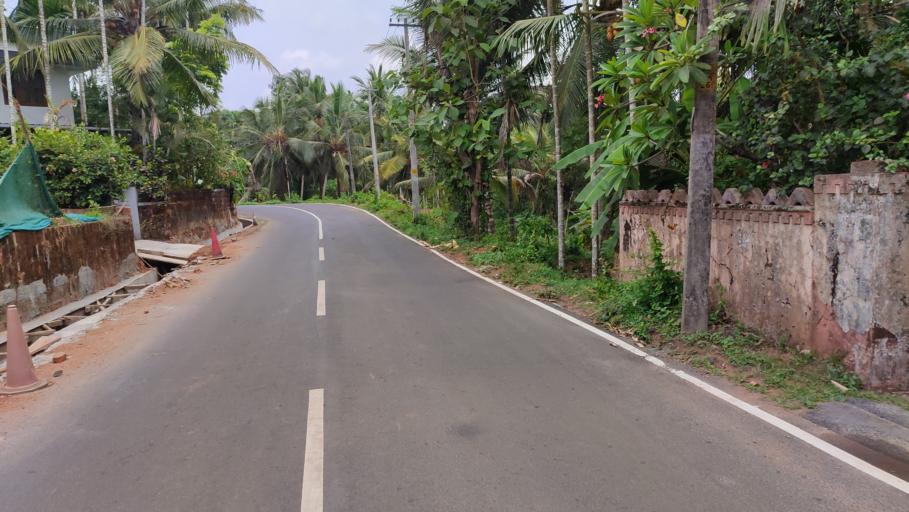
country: IN
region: Kerala
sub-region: Kasaragod District
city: Kannangad
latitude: 12.3201
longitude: 75.1134
